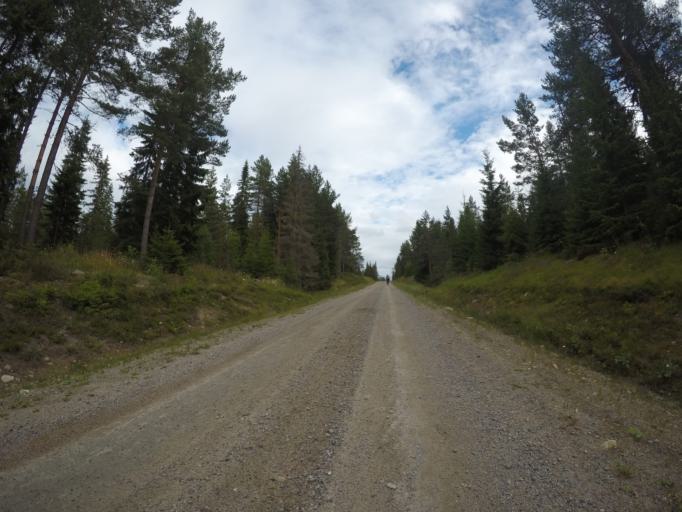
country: SE
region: OErebro
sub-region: Hallefors Kommun
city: Haellefors
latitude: 60.0137
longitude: 14.4458
